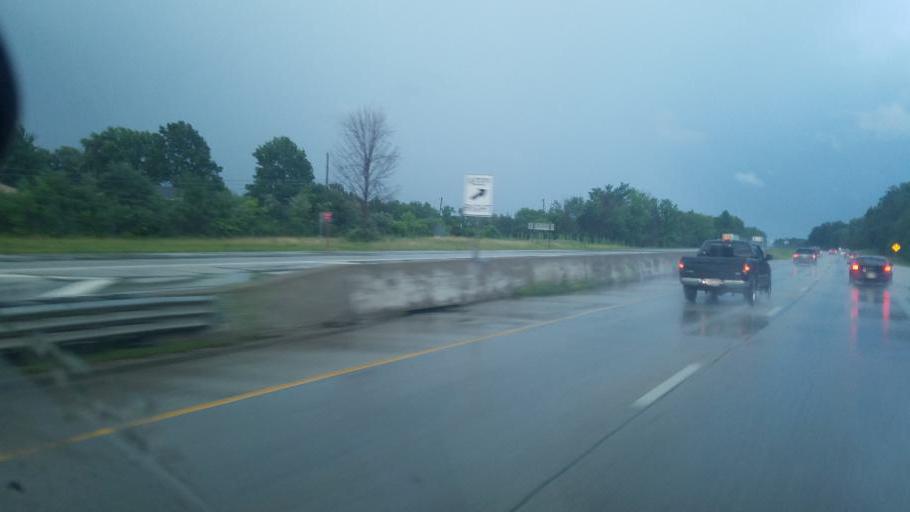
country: US
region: Ohio
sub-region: Wayne County
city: Doylestown
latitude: 40.9883
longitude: -81.6637
